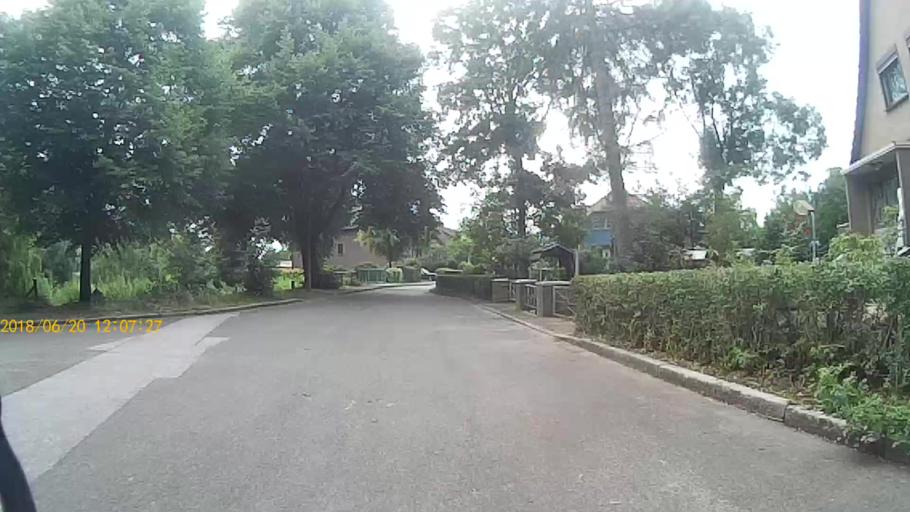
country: DE
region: Hamburg
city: Harburg
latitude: 53.4877
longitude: 10.0087
